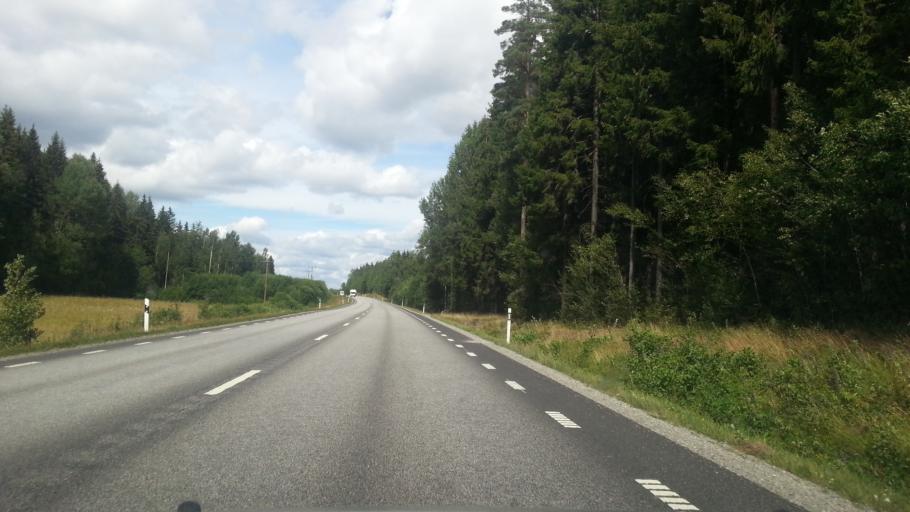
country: SE
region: OErebro
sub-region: Lindesbergs Kommun
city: Lindesberg
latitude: 59.5768
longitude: 15.2043
